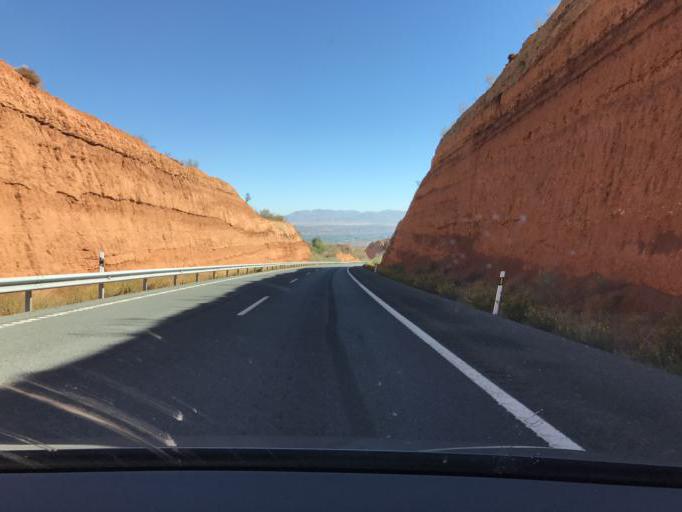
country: ES
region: Andalusia
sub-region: Provincia de Granada
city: Darro
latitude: 37.3236
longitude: -3.2560
